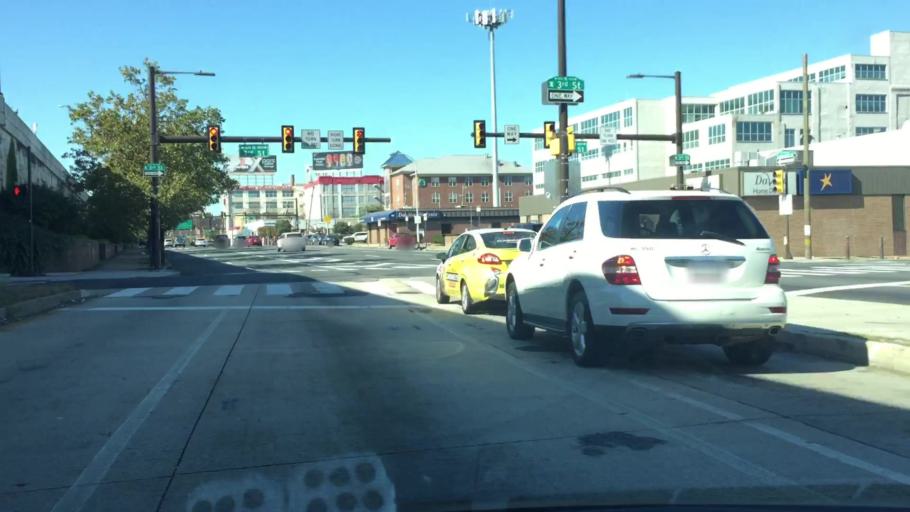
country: US
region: Pennsylvania
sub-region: Philadelphia County
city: Philadelphia
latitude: 39.9573
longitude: -75.1439
